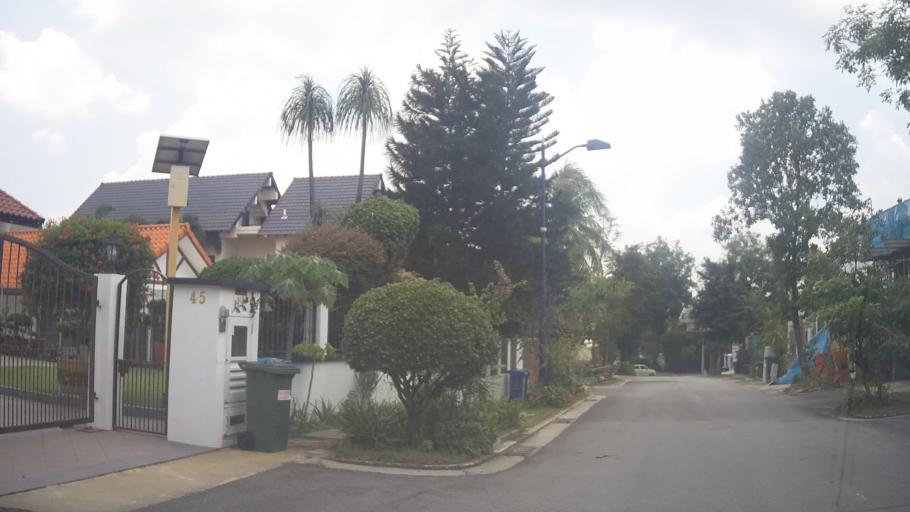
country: SG
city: Singapore
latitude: 1.3641
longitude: 103.8708
